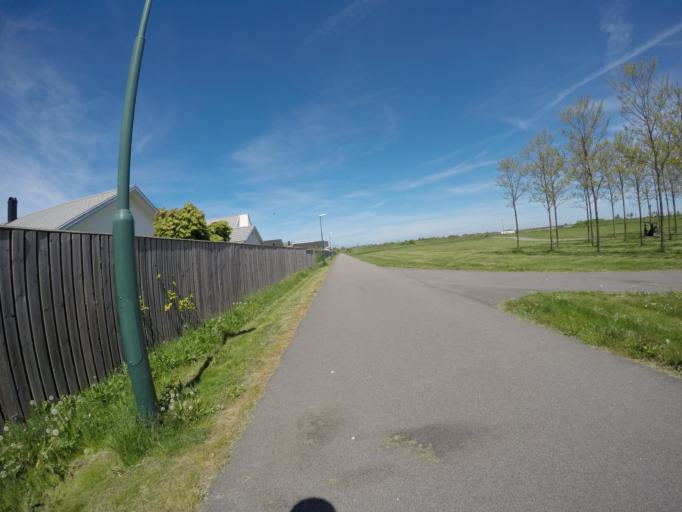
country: SE
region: Skane
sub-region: Malmo
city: Bunkeflostrand
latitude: 55.5600
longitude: 12.9263
